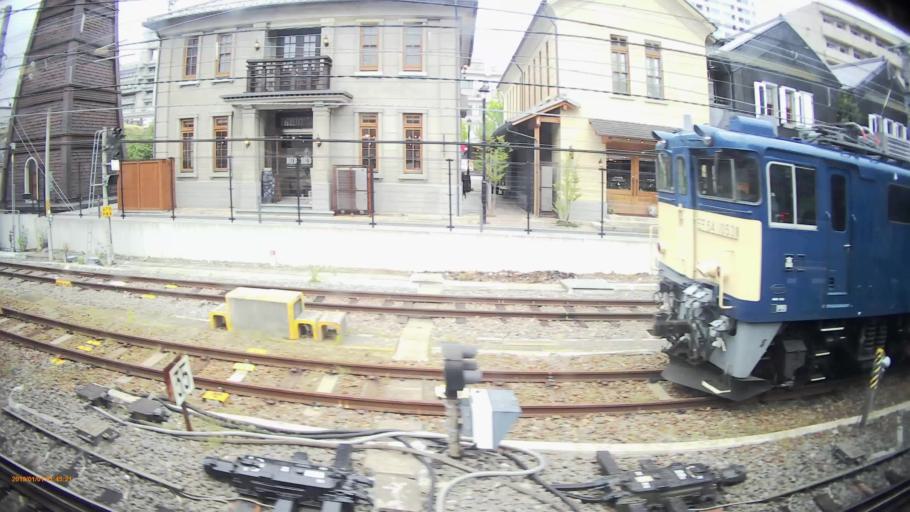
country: JP
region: Yamanashi
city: Kofu-shi
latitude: 35.6666
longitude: 138.5716
